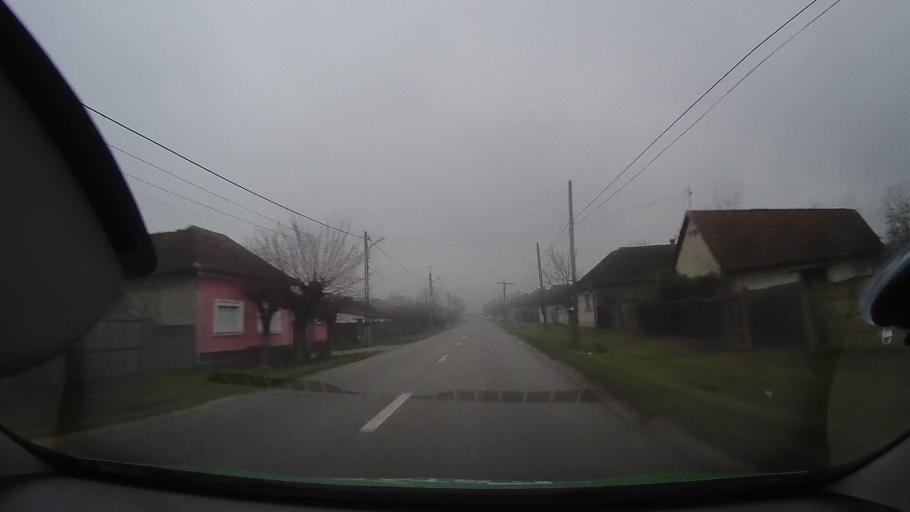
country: RO
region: Bihor
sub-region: Comuna Tinca
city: Gurbediu
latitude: 46.7865
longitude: 21.8673
